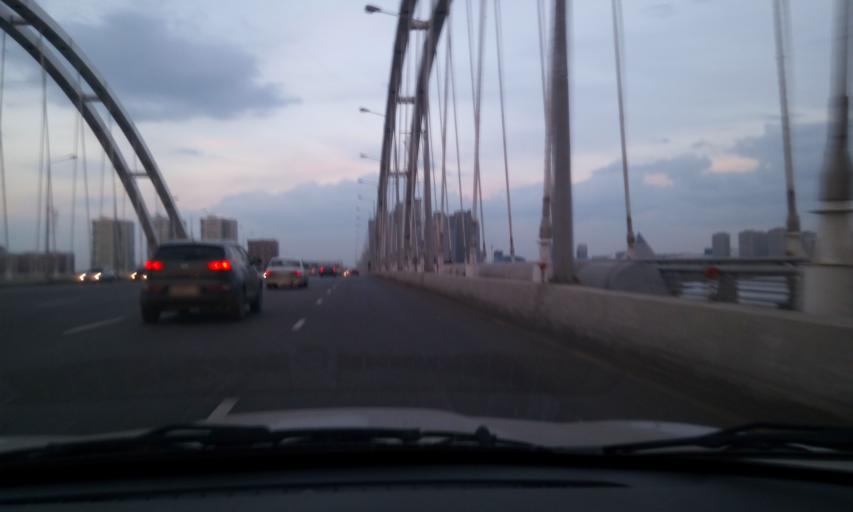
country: KZ
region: Astana Qalasy
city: Astana
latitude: 51.1313
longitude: 71.4462
